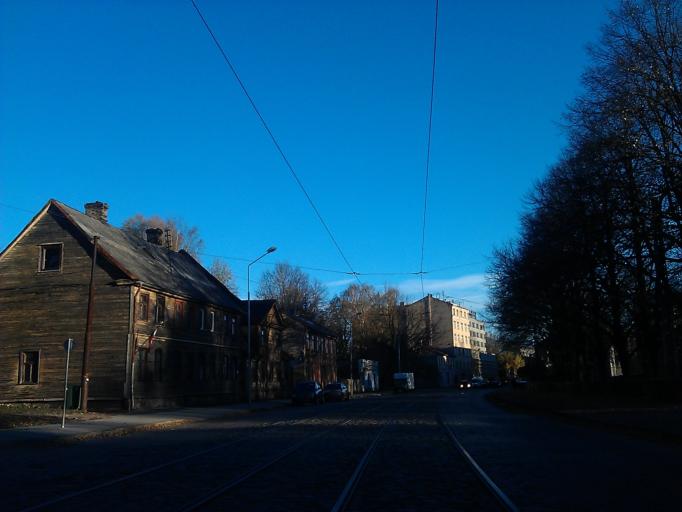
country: LV
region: Riga
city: Riga
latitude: 56.9372
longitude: 24.1530
